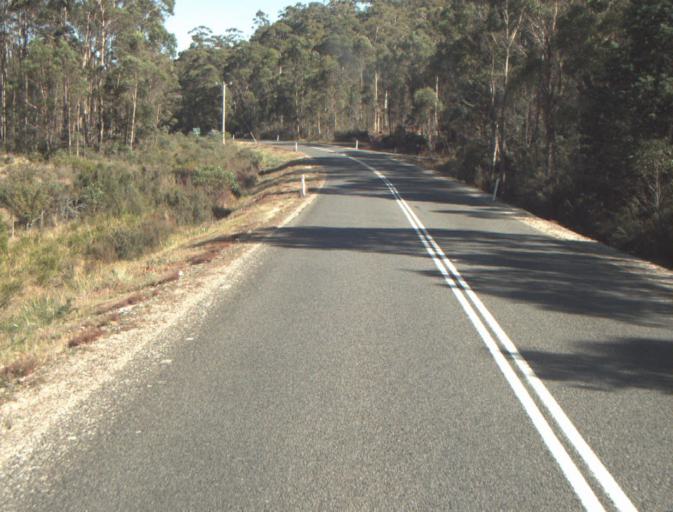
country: AU
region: Tasmania
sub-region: Launceston
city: Mayfield
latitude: -41.3299
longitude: 147.1804
